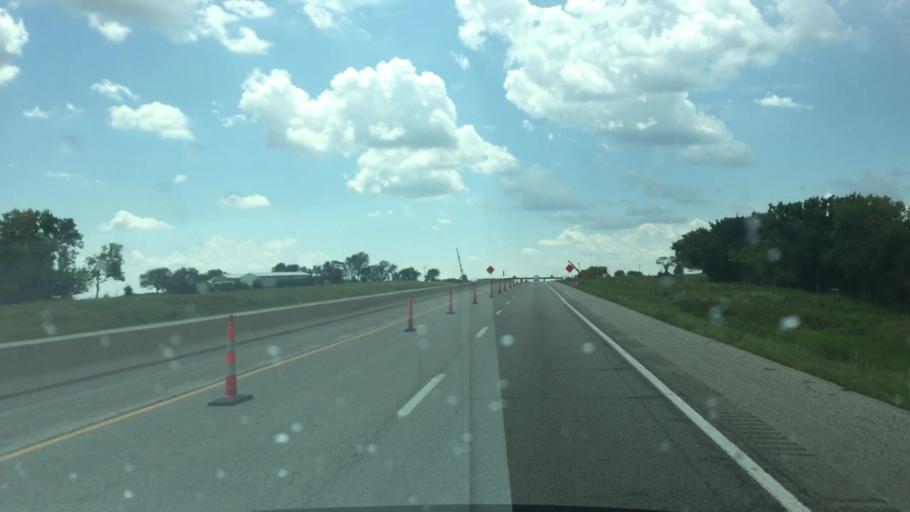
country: US
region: Kansas
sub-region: Shawnee County
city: Auburn
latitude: 38.9168
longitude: -95.7801
